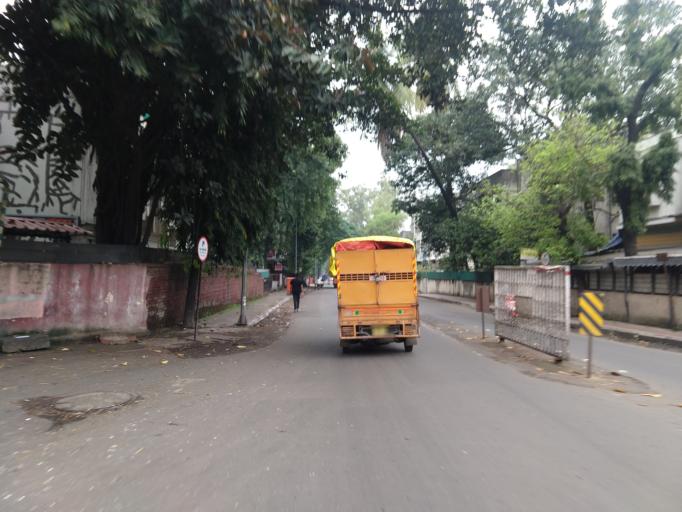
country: IN
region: Maharashtra
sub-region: Pune Division
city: Pune
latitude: 18.5042
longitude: 73.8524
